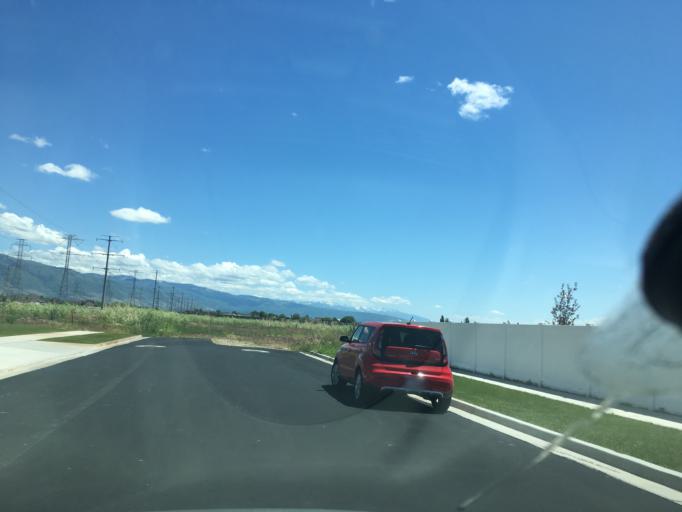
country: US
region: Utah
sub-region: Davis County
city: Layton
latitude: 41.0528
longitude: -112.0045
